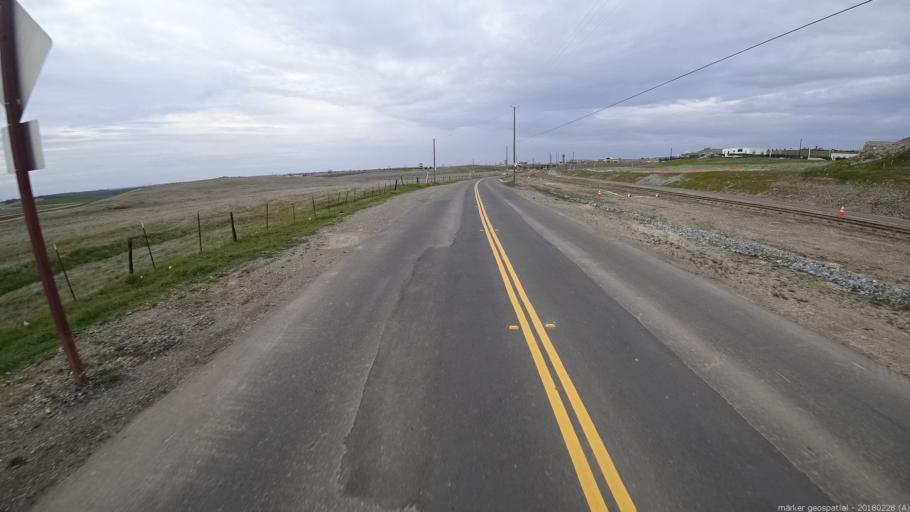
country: US
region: California
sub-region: El Dorado County
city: El Dorado Hills
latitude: 38.6387
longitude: -121.1056
